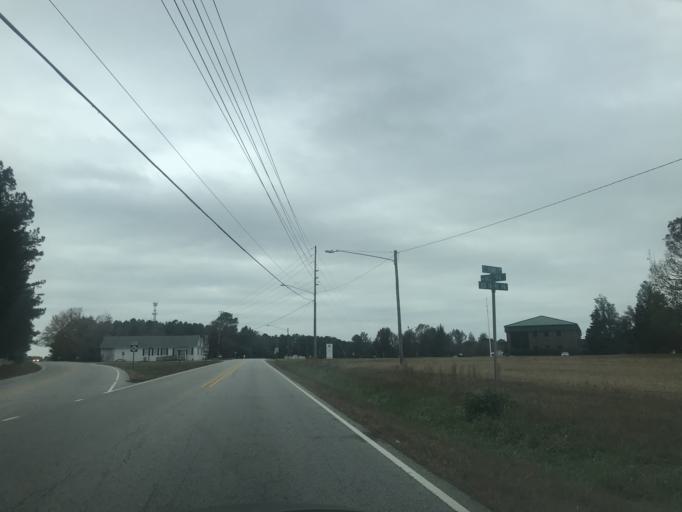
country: US
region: North Carolina
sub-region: Franklin County
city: Youngsville
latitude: 36.0327
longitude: -78.4833
